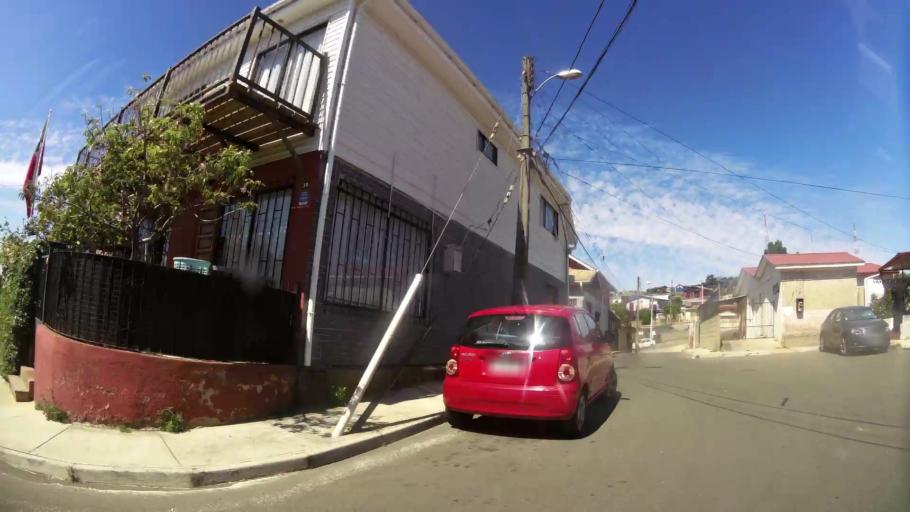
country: CL
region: Valparaiso
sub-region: Provincia de Valparaiso
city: Vina del Mar
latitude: -33.0424
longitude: -71.5725
